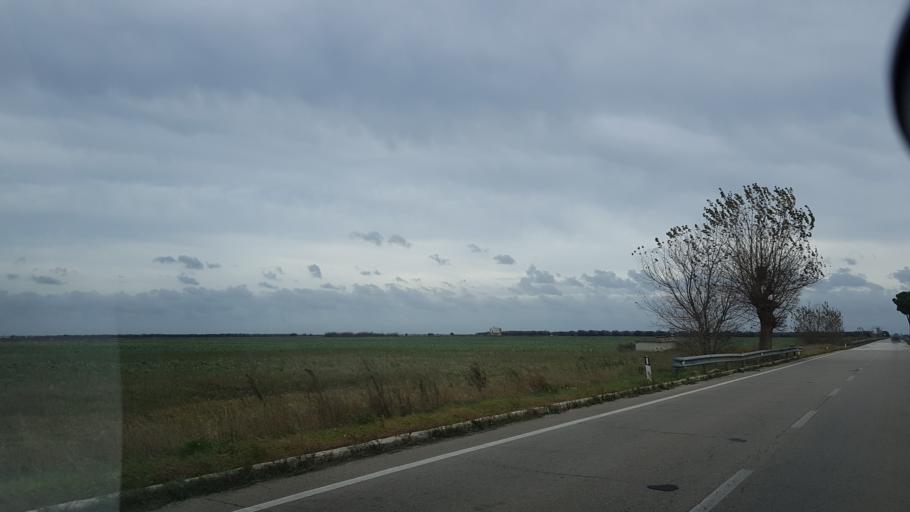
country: IT
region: Apulia
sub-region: Provincia di Brindisi
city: San Pancrazio Salentino
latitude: 40.4110
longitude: 17.8691
